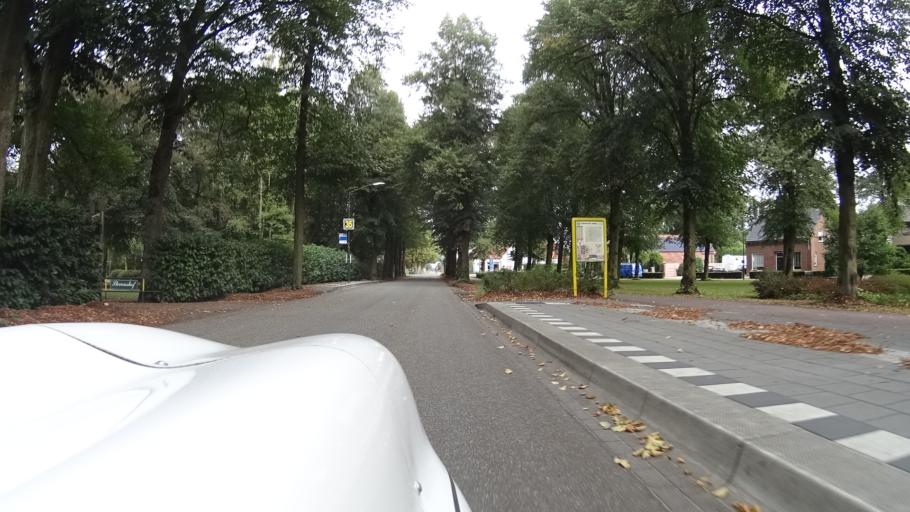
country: NL
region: North Brabant
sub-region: Gemeente Sint Anthonis
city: Sint Anthonis
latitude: 51.6024
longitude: 5.9162
